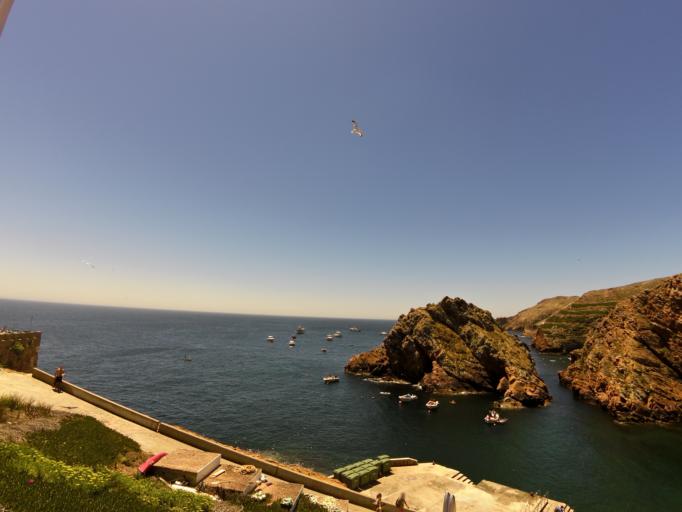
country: PT
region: Leiria
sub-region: Peniche
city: Peniche
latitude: 39.4144
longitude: -9.5061
